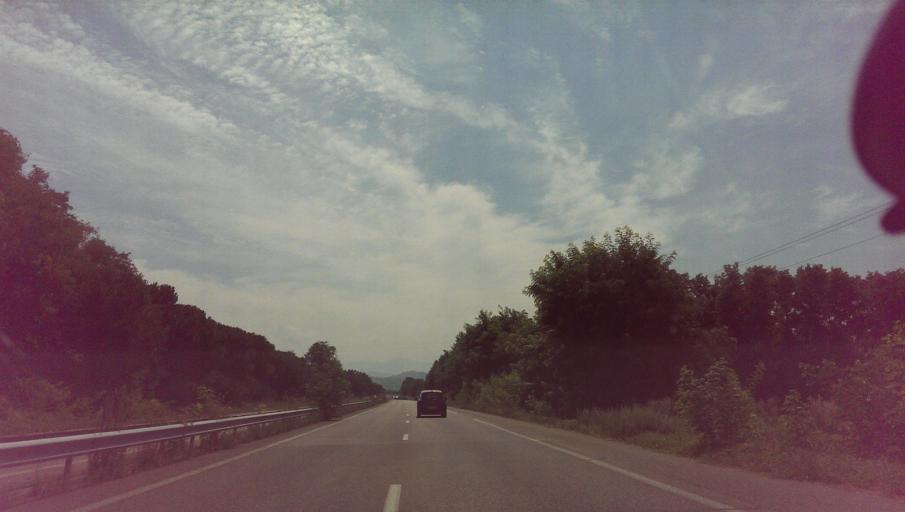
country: FR
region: Midi-Pyrenees
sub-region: Departement de l'Ariege
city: Saint-Jean-du-Falga
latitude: 43.0874
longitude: 1.6348
